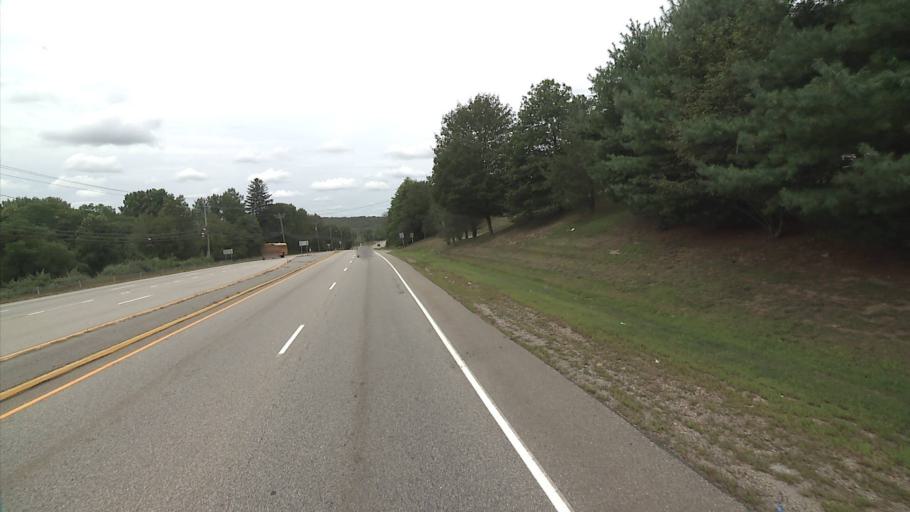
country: US
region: Connecticut
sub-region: New London County
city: Central Waterford
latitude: 41.3792
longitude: -72.1498
